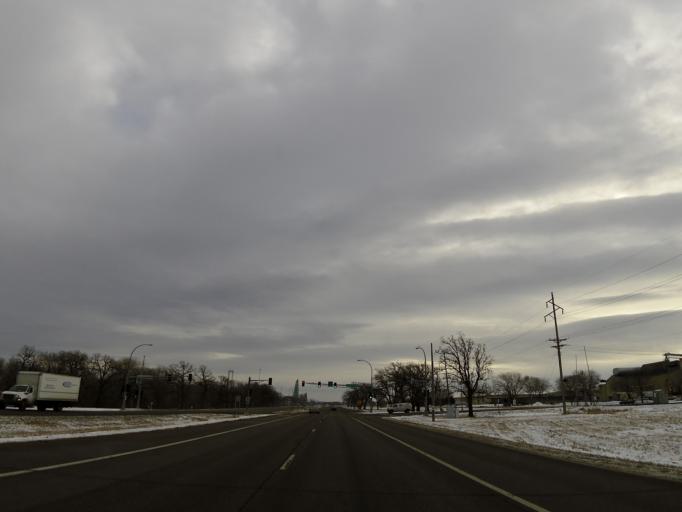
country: US
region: Minnesota
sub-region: Hennepin County
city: Eden Prairie
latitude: 44.8002
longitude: -93.4710
